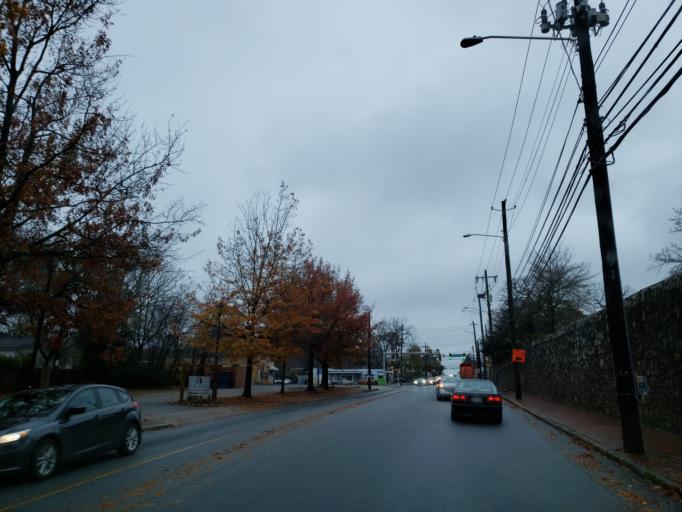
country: US
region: Georgia
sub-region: Fulton County
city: Atlanta
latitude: 33.7478
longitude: -84.3682
